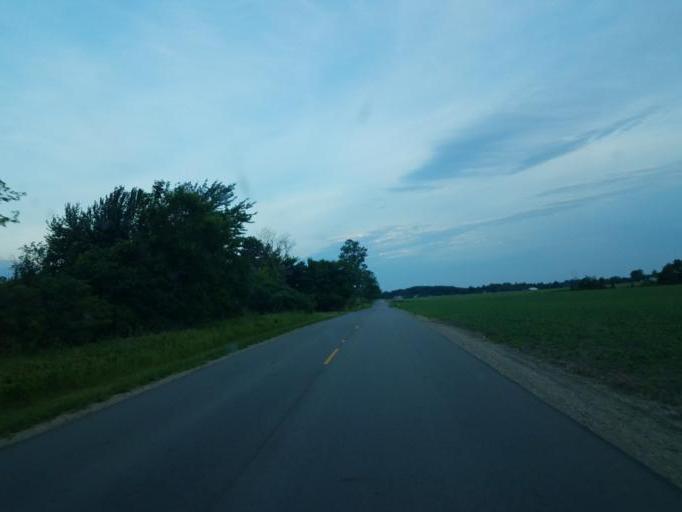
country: US
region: Michigan
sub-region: Eaton County
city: Charlotte
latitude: 42.5971
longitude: -84.8420
